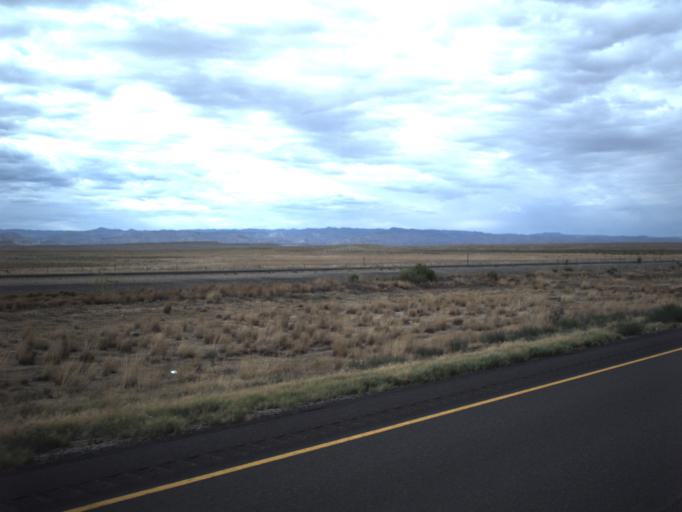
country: US
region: Colorado
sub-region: Mesa County
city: Loma
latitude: 39.0698
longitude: -109.2401
